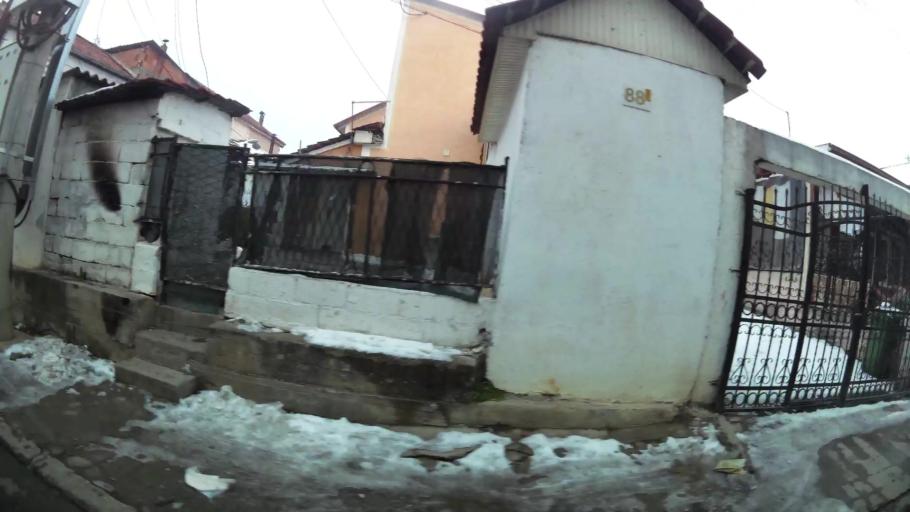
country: MK
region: Suto Orizari
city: Suto Orizare
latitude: 42.0426
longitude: 21.4246
